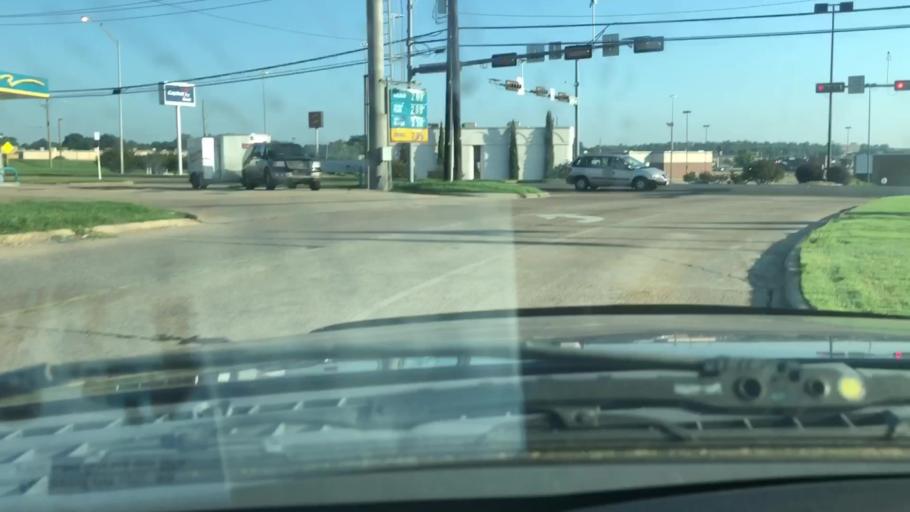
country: US
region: Texas
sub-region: Bowie County
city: Wake Village
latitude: 33.4538
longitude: -94.0844
